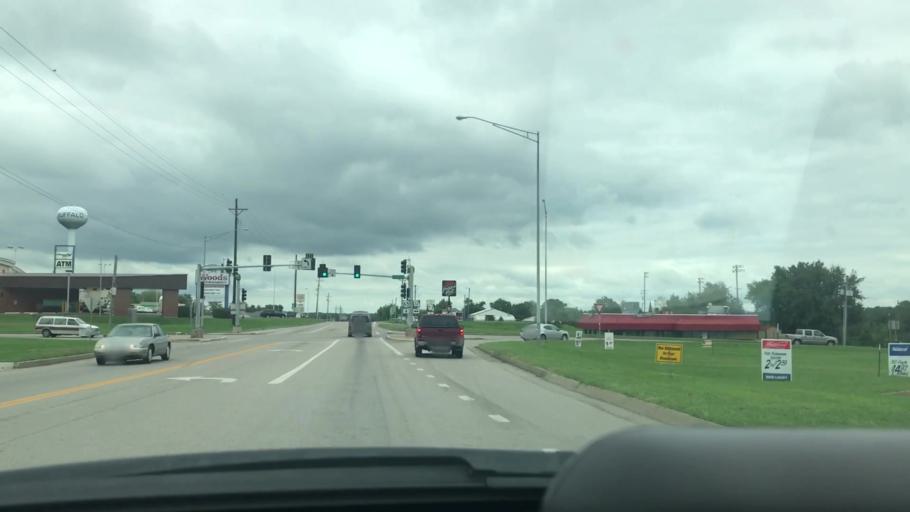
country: US
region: Missouri
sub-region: Dallas County
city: Buffalo
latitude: 37.6399
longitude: -93.1042
